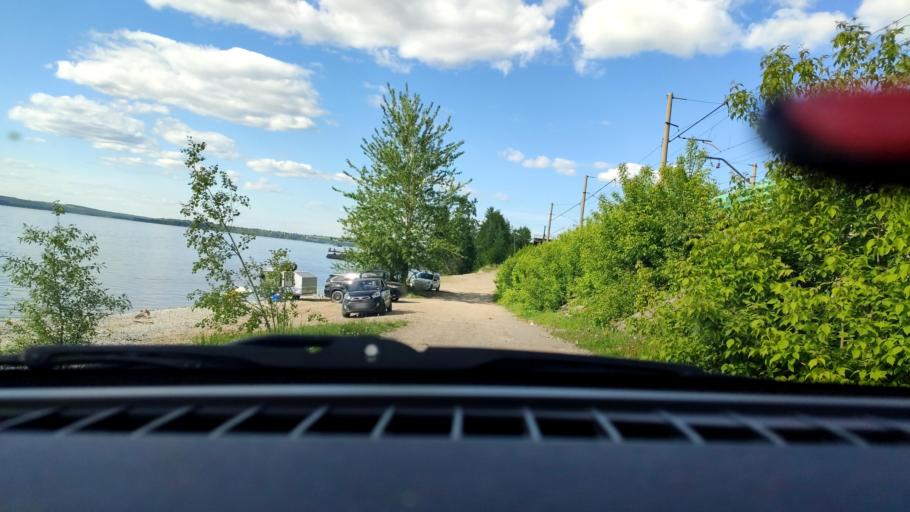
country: RU
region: Perm
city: Perm
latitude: 58.1202
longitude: 56.3663
